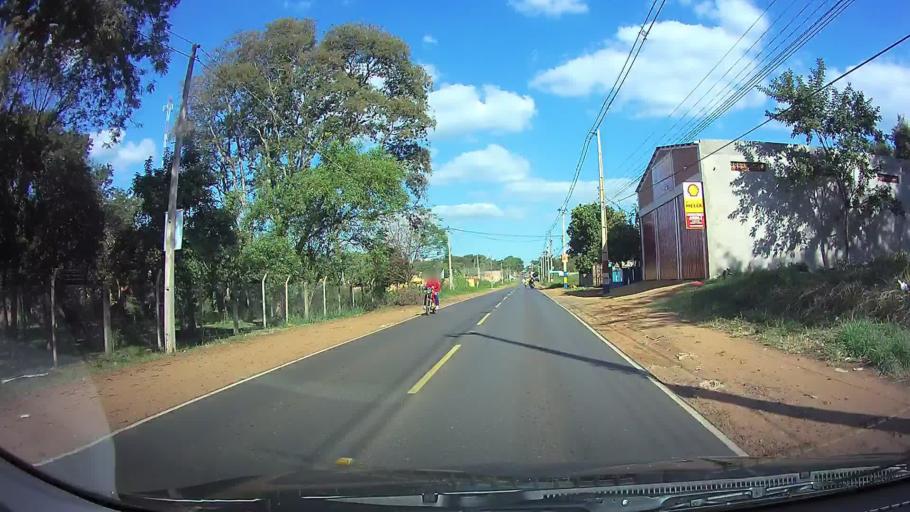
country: PY
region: Central
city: Limpio
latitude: -25.2271
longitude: -57.4769
